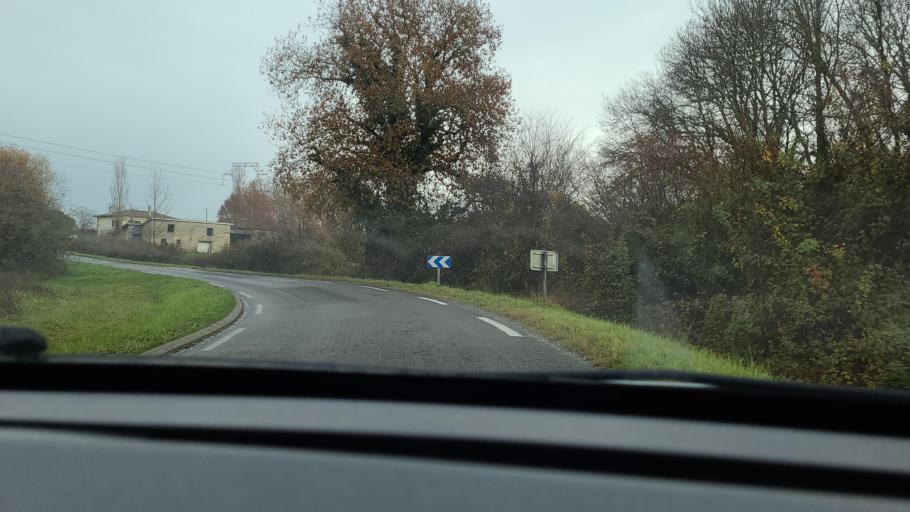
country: FR
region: Aquitaine
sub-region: Departement de la Gironde
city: Tauriac
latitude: 45.0440
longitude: -0.5057
